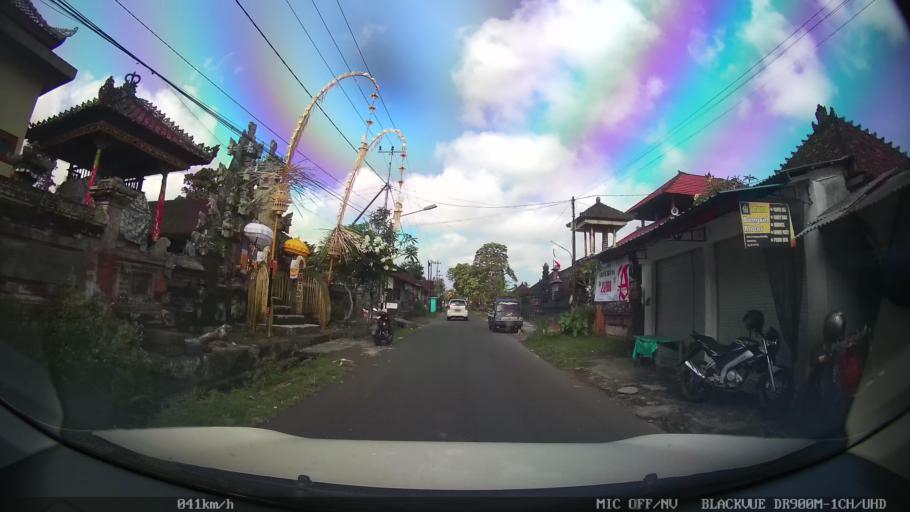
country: ID
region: Bali
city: Banjar Apuan Kaja
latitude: -8.5145
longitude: 115.3258
